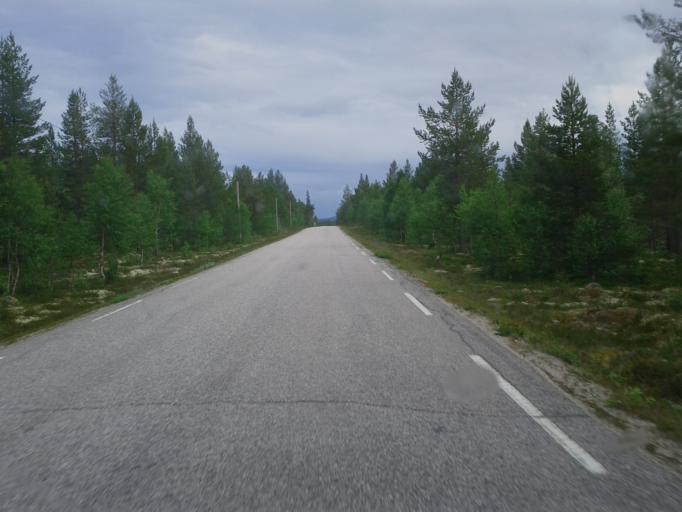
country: NO
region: Hedmark
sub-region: Engerdal
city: Engerdal
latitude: 62.0458
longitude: 11.6927
